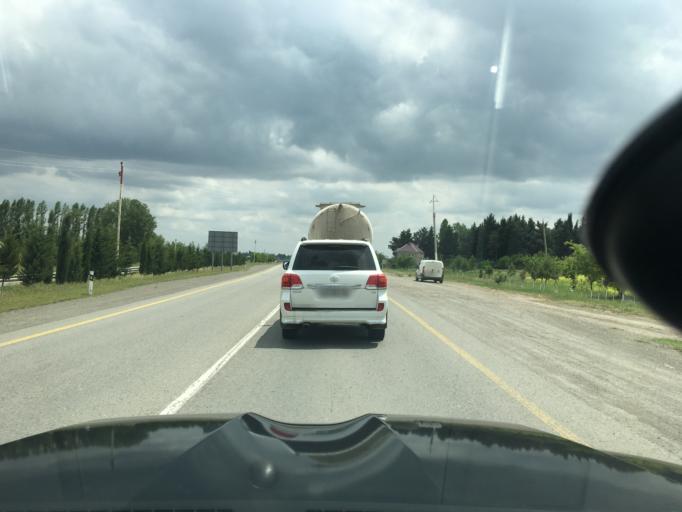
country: AZ
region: Tovuz
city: Qaraxanli
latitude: 41.0294
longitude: 45.6010
